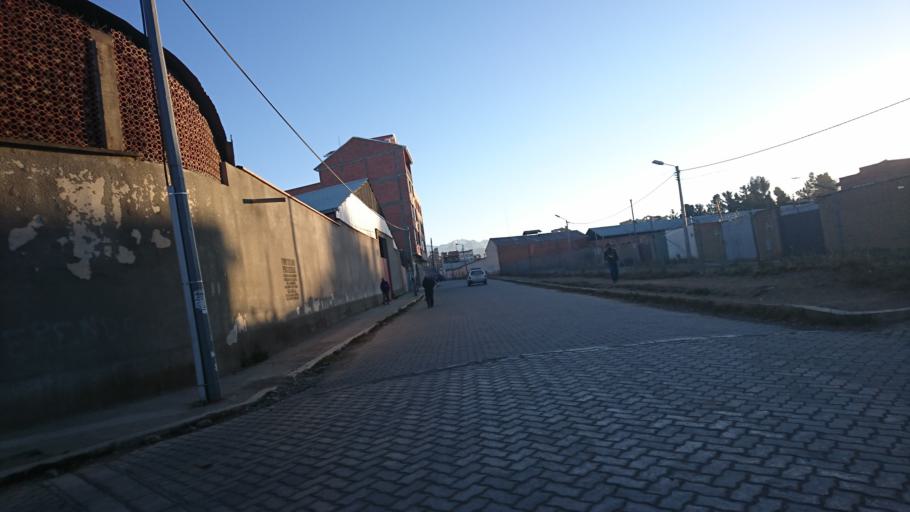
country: BO
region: La Paz
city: La Paz
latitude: -16.4986
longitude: -68.1885
